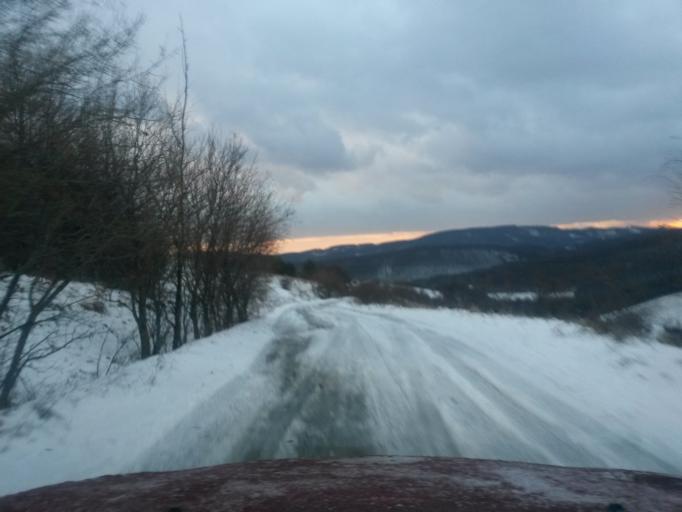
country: SK
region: Kosicky
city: Kosice
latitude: 48.7519
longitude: 21.1237
